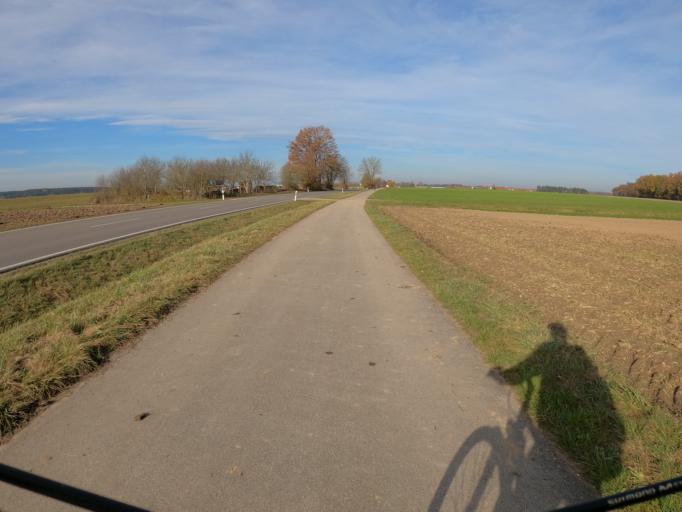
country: DE
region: Bavaria
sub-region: Swabia
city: Leipheim
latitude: 48.4047
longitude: 10.1985
